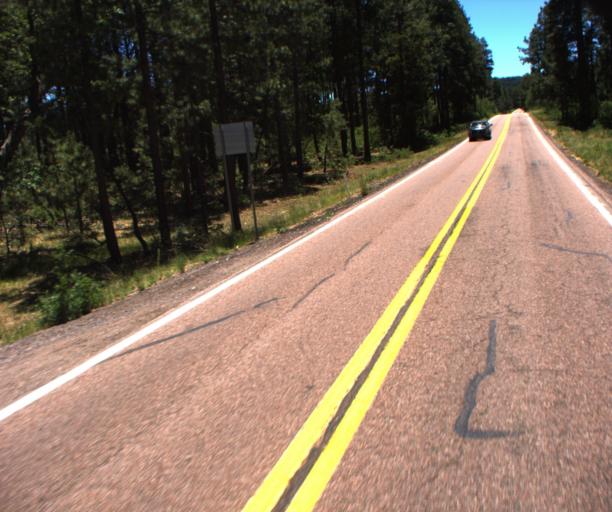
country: US
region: Arizona
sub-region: Gila County
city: Pine
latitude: 34.4786
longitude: -111.3813
